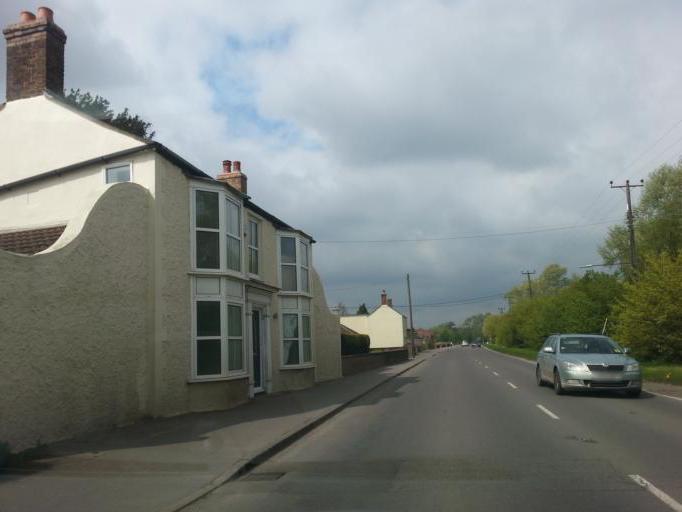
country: GB
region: England
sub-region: Norfolk
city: Outwell
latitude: 52.6132
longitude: 0.2325
